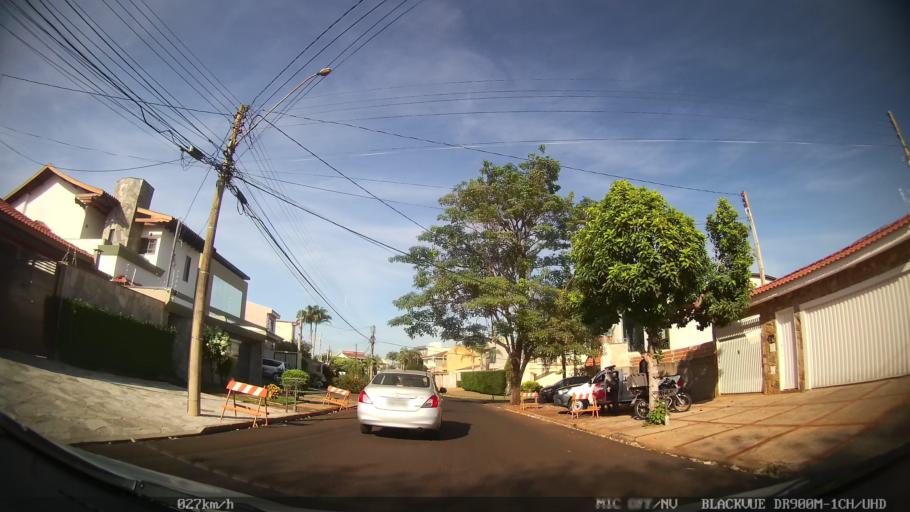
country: BR
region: Sao Paulo
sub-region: Ribeirao Preto
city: Ribeirao Preto
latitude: -21.1983
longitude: -47.8182
